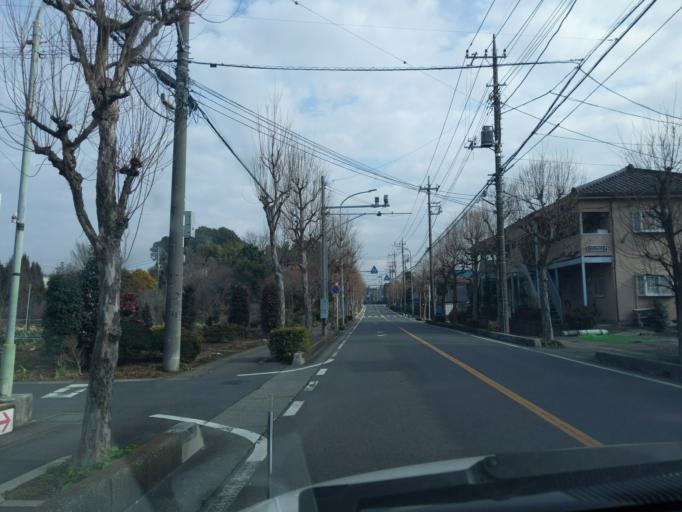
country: JP
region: Saitama
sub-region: Kawaguchi-shi
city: Hatogaya-honcho
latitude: 35.8609
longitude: 139.7298
